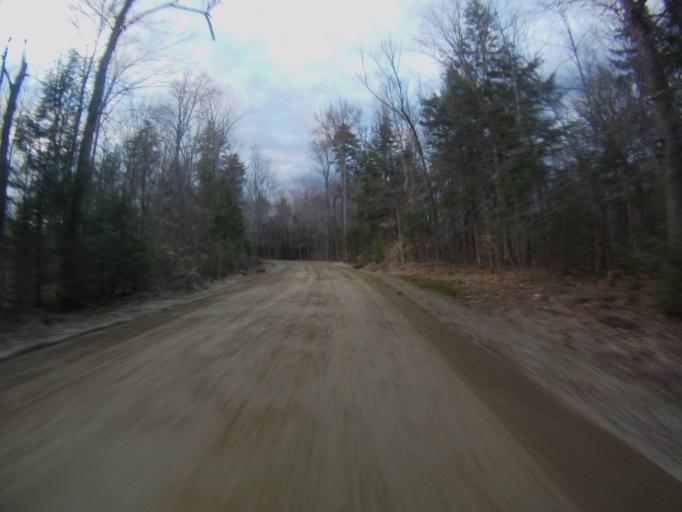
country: US
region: Vermont
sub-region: Rutland County
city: Brandon
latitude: 43.9357
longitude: -73.0207
